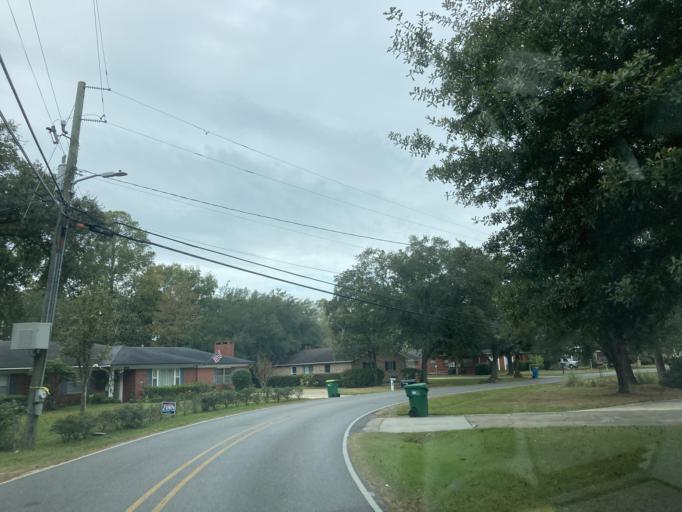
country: US
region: Mississippi
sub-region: Jackson County
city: Gulf Hills
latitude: 30.4318
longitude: -88.8403
